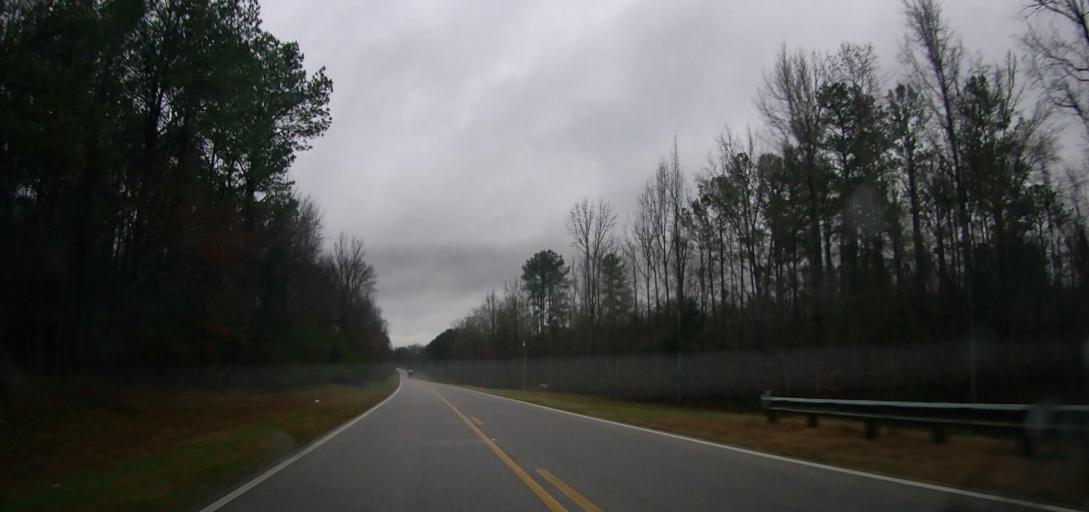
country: US
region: Alabama
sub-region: Bibb County
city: Centreville
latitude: 32.9112
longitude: -87.0230
